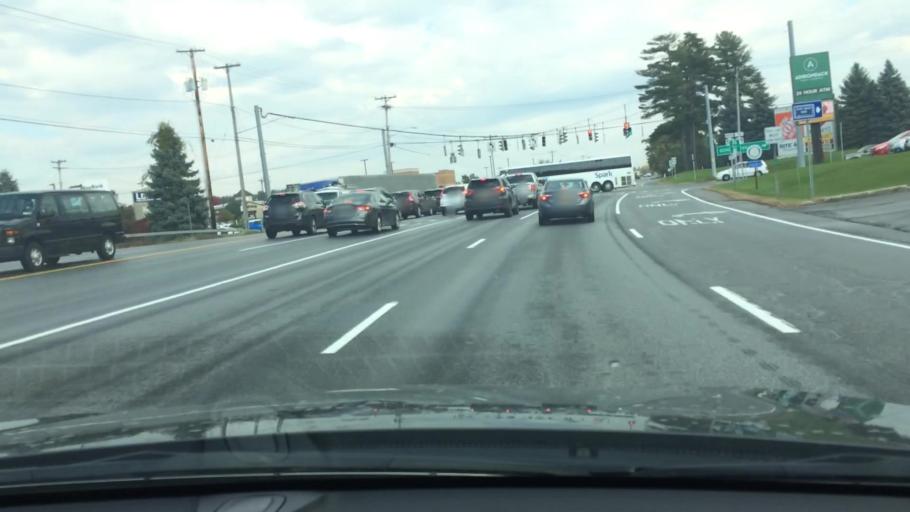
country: US
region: New York
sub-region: Saratoga County
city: Saratoga Springs
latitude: 43.1000
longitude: -73.7479
